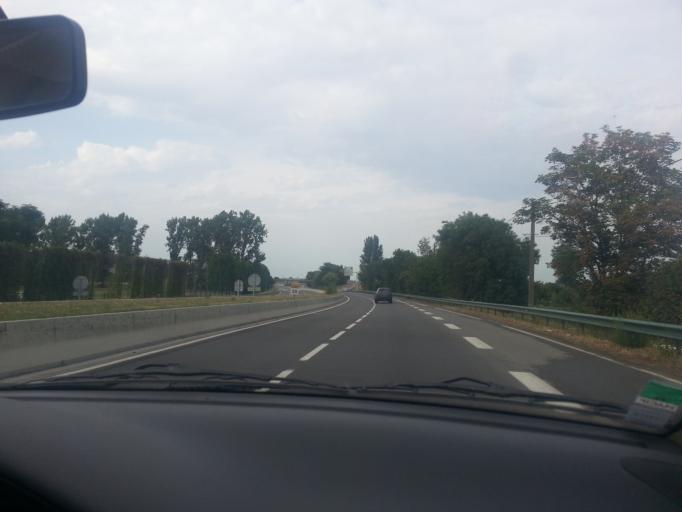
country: FR
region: Auvergne
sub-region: Departement du Puy-de-Dome
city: Cebazat
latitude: 45.8247
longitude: 3.1117
